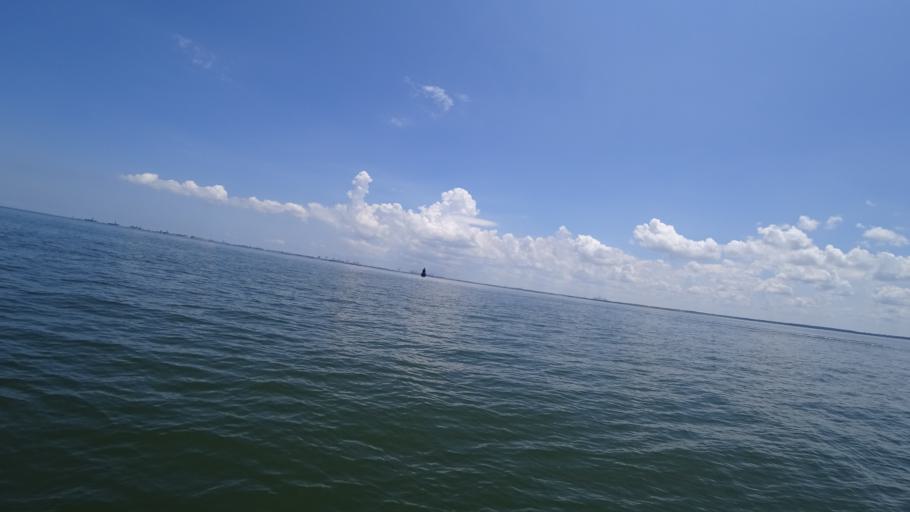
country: US
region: Virginia
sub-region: City of Newport News
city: Newport News
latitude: 36.9488
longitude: -76.3979
